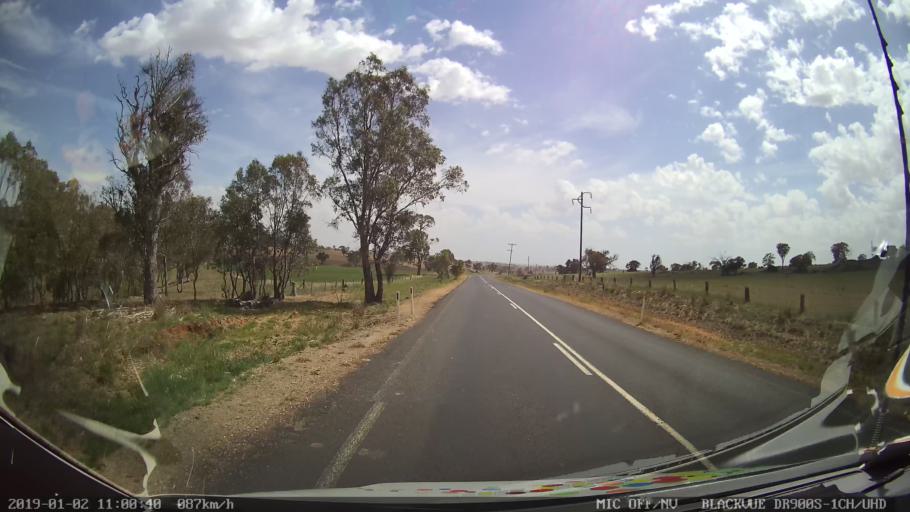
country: AU
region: New South Wales
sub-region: Cootamundra
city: Cootamundra
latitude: -34.6058
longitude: 148.3125
